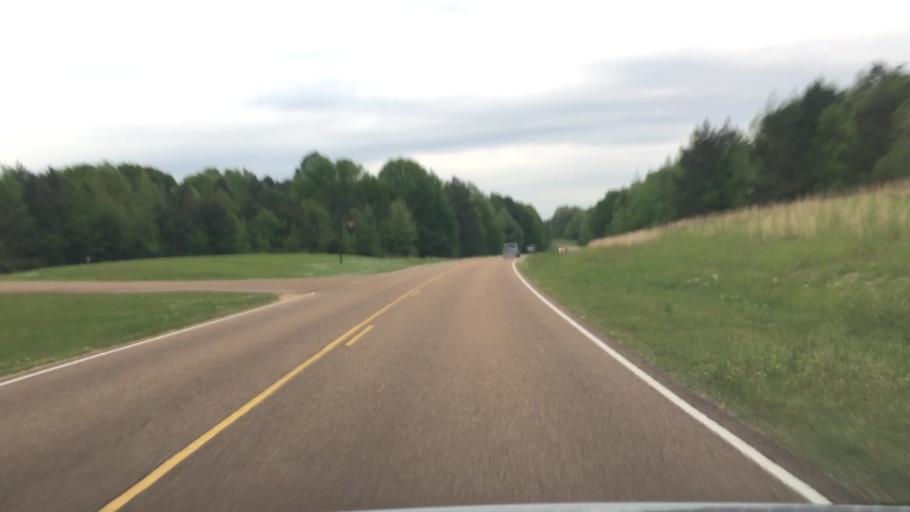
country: US
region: Mississippi
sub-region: Hinds County
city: Clinton
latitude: 32.3882
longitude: -90.2556
